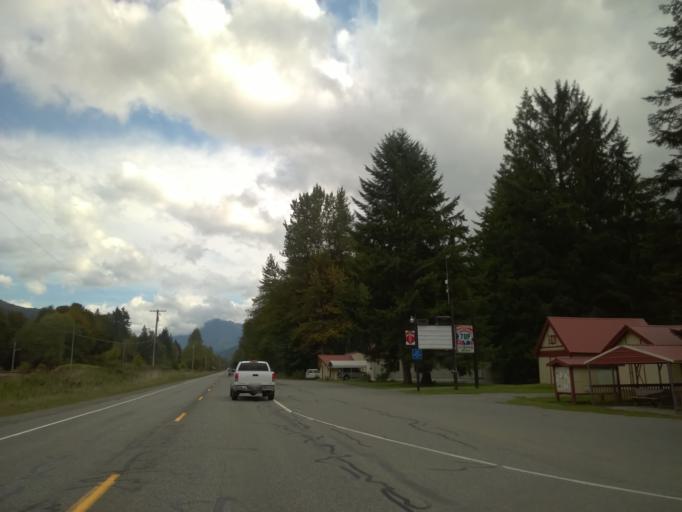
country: US
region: Washington
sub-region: Snohomish County
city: Gold Bar
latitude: 47.7725
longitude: -121.4857
